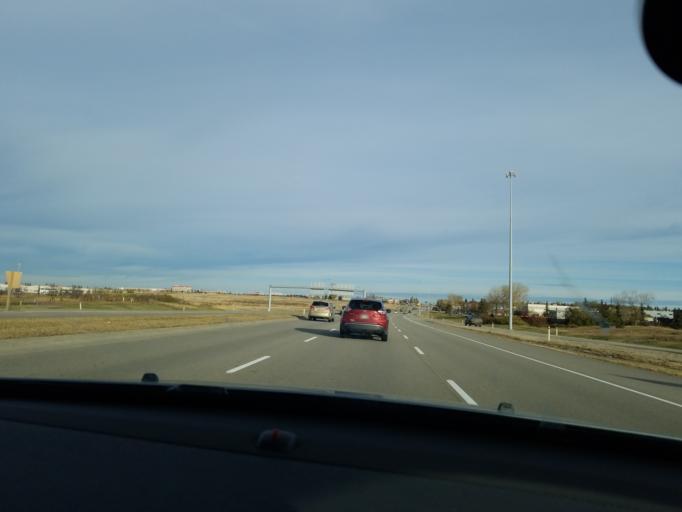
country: CA
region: Alberta
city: Sherwood Park
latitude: 53.5409
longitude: -113.3343
